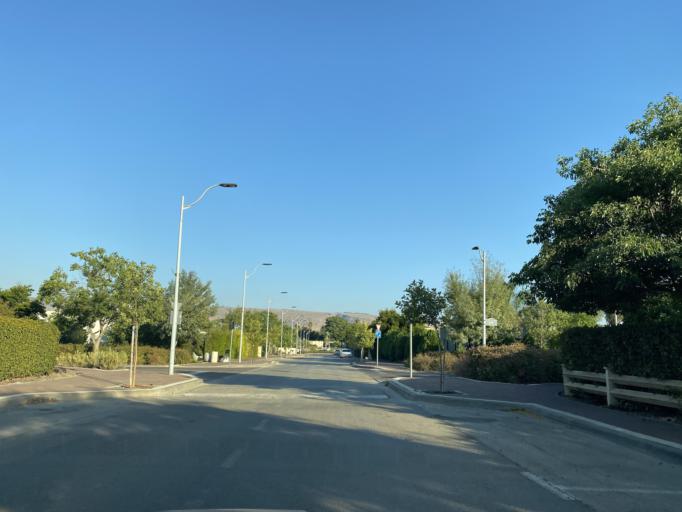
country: IL
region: Northern District
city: Qiryat Shemona
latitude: 33.1760
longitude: 35.6049
